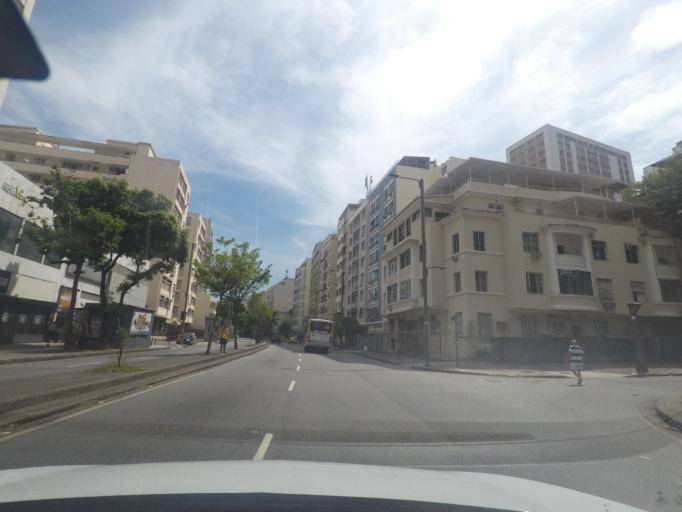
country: BR
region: Rio de Janeiro
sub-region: Rio De Janeiro
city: Rio de Janeiro
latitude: -22.9310
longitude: -43.2383
